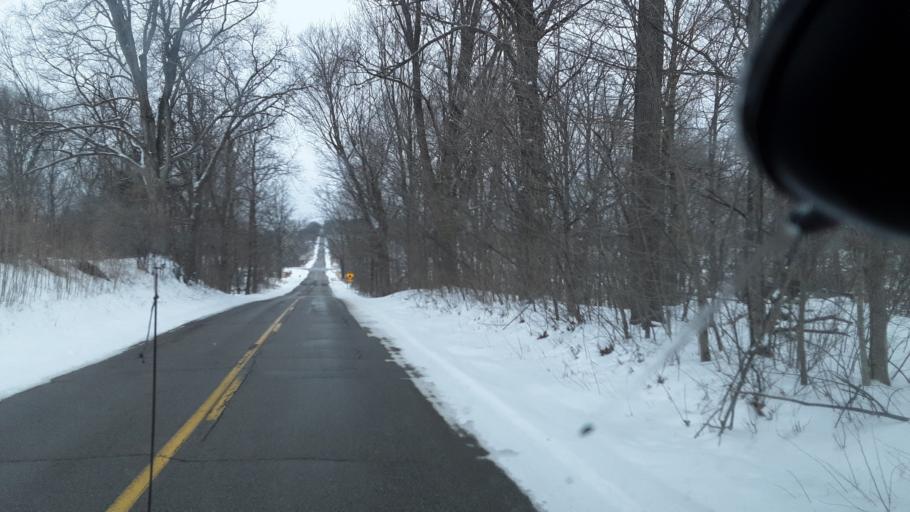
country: US
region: Michigan
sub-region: Ingham County
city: Leslie
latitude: 42.4501
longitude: -84.3941
